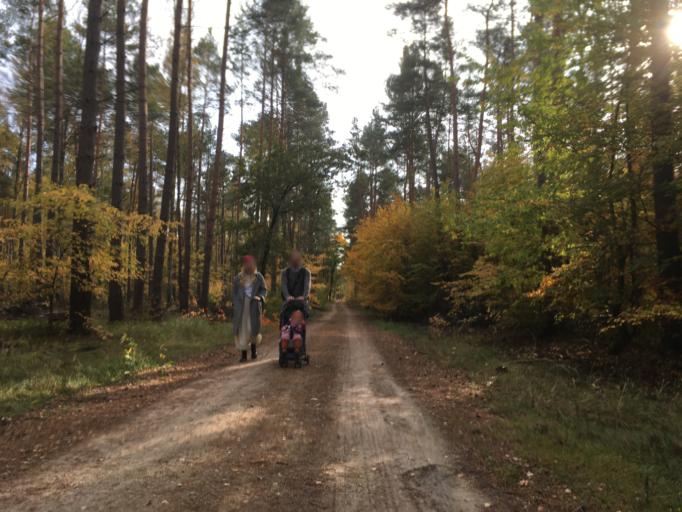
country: DE
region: Brandenburg
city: Liebenwalde
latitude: 52.9336
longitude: 13.5032
